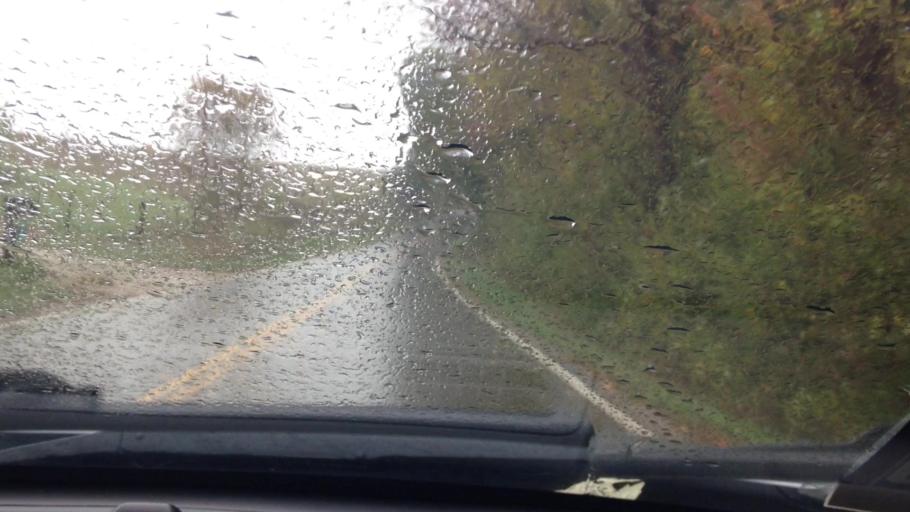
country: US
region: Kansas
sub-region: Leavenworth County
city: Lansing
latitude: 39.2121
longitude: -94.8395
